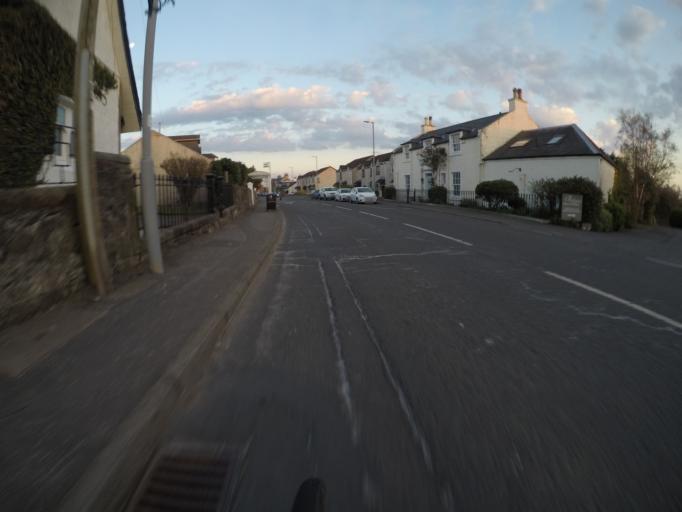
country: GB
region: Scotland
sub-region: South Ayrshire
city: Troon
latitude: 55.5516
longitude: -4.6253
